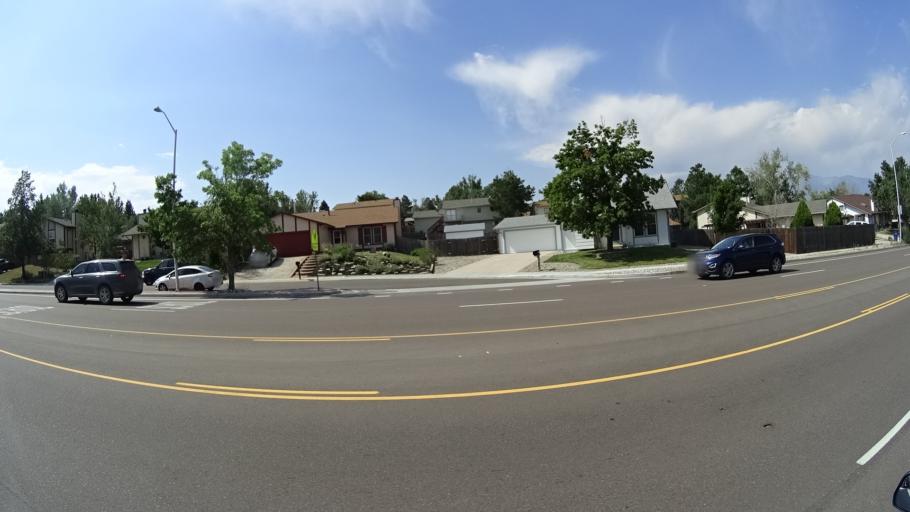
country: US
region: Colorado
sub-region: El Paso County
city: Cimarron Hills
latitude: 38.9249
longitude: -104.7688
